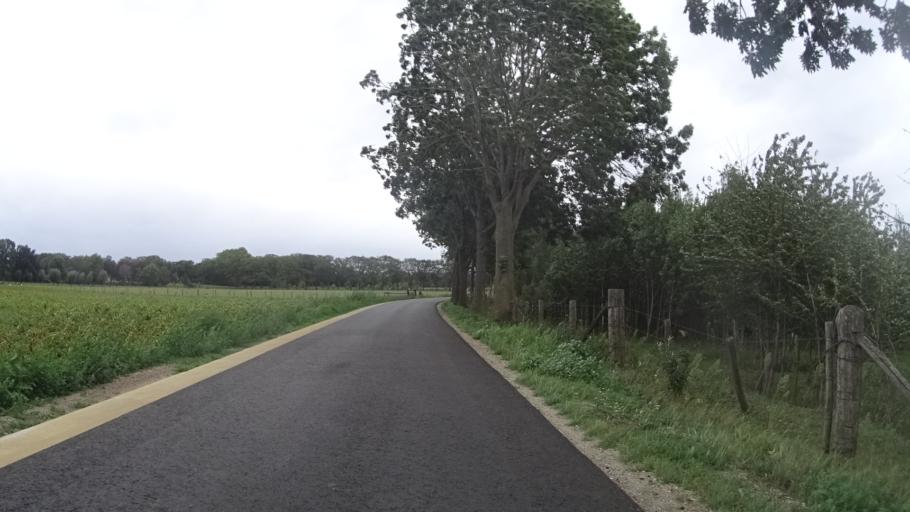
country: NL
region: Limburg
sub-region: Gemeente Venlo
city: Tegelen
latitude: 51.3374
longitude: 6.1138
